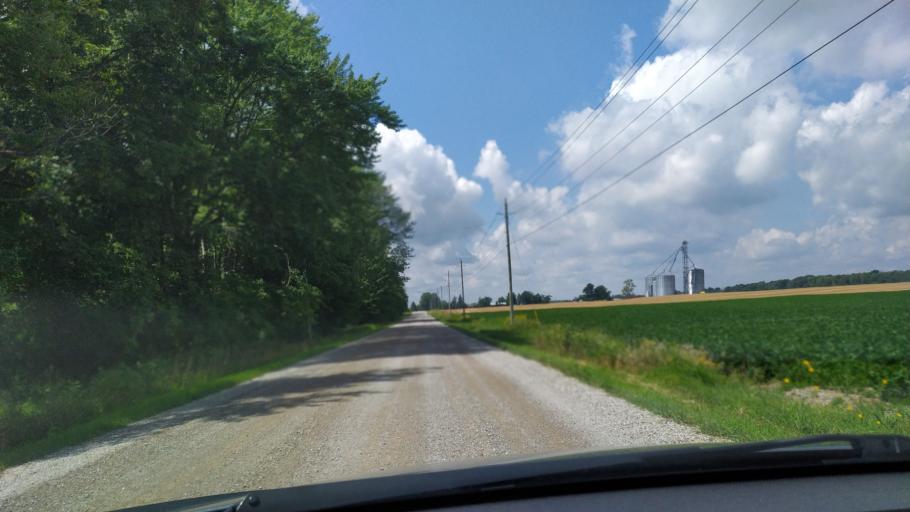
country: CA
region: Ontario
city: London
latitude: 43.0792
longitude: -81.3342
